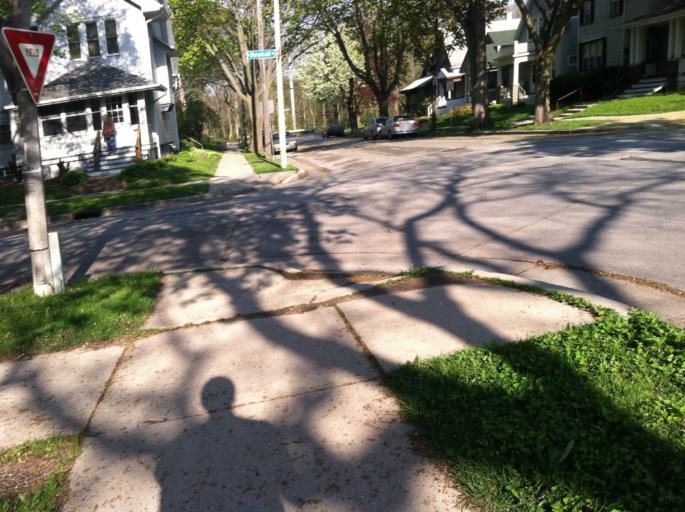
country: US
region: Wisconsin
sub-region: Milwaukee County
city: Shorewood
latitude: 43.0794
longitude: -87.8900
